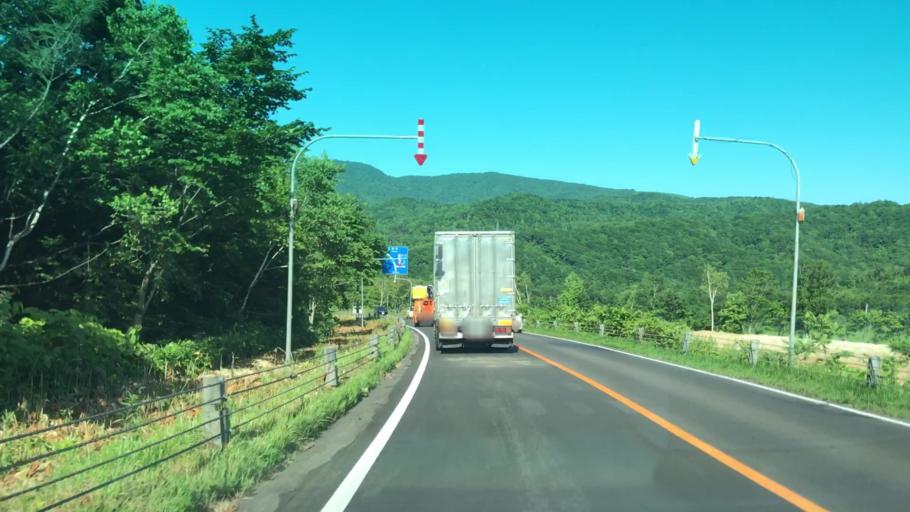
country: JP
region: Hokkaido
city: Yoichi
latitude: 43.0741
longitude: 140.7069
